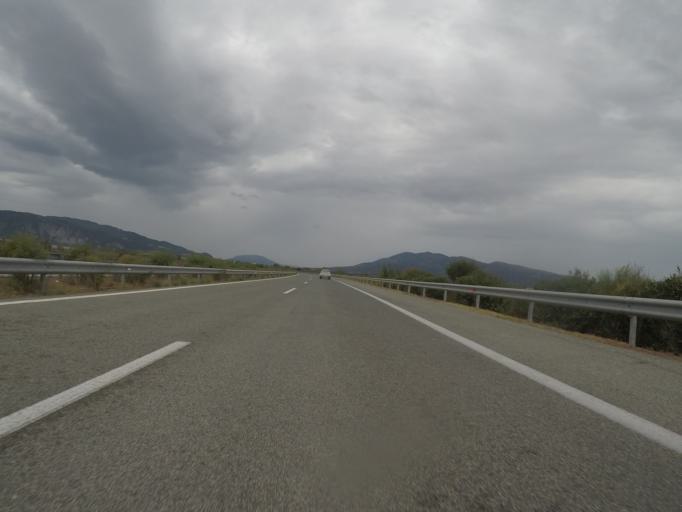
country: GR
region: West Greece
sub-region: Nomos Aitolias kai Akarnanias
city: Lepenou
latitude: 38.6566
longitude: 21.2439
